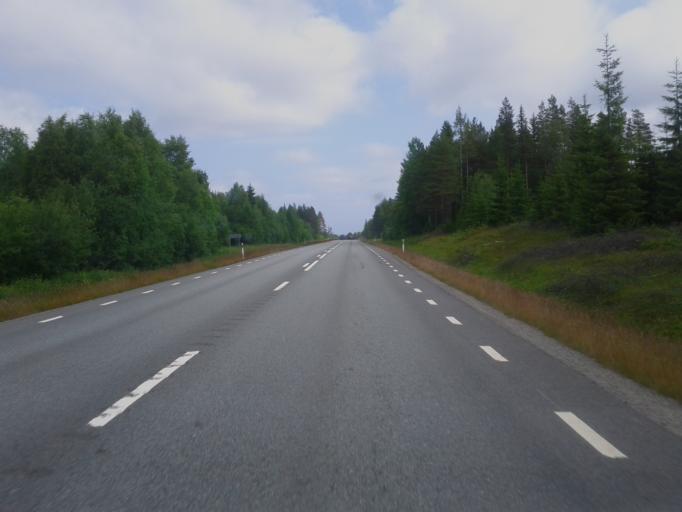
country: SE
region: Vaesterbotten
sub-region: Skelleftea Kommun
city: Burea
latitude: 64.3411
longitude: 21.2791
